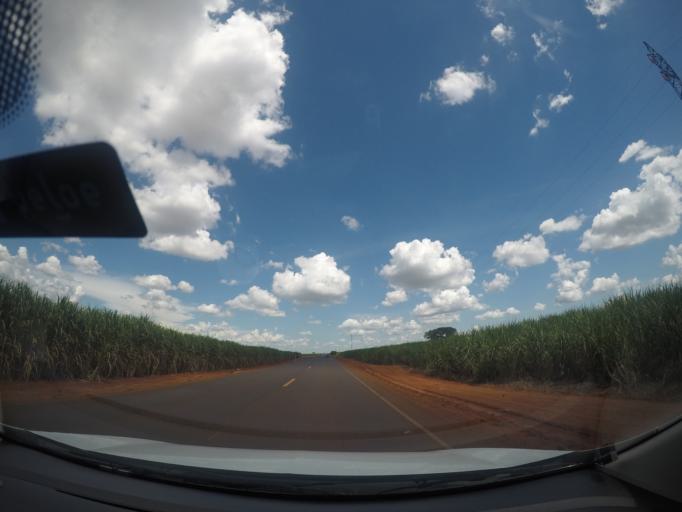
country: BR
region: Minas Gerais
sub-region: Frutal
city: Frutal
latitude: -19.8565
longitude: -48.7336
